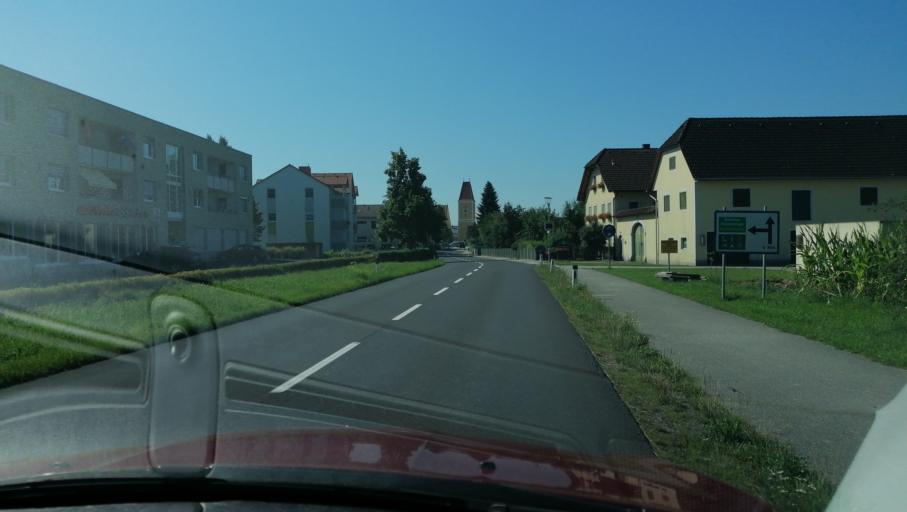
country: AT
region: Upper Austria
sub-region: Politischer Bezirk Urfahr-Umgebung
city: Feldkirchen an der Donau
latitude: 48.3477
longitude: 14.0525
